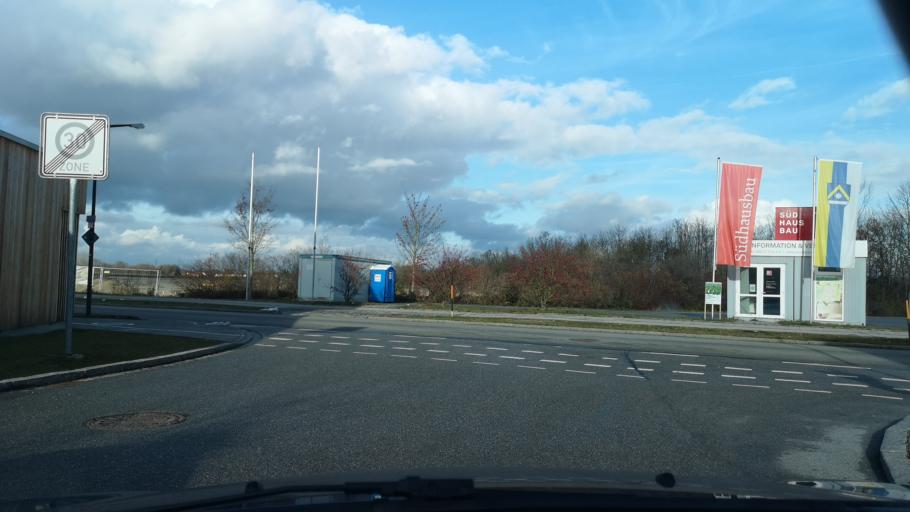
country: DE
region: Bavaria
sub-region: Upper Bavaria
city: Pliening
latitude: 48.1807
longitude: 11.8023
